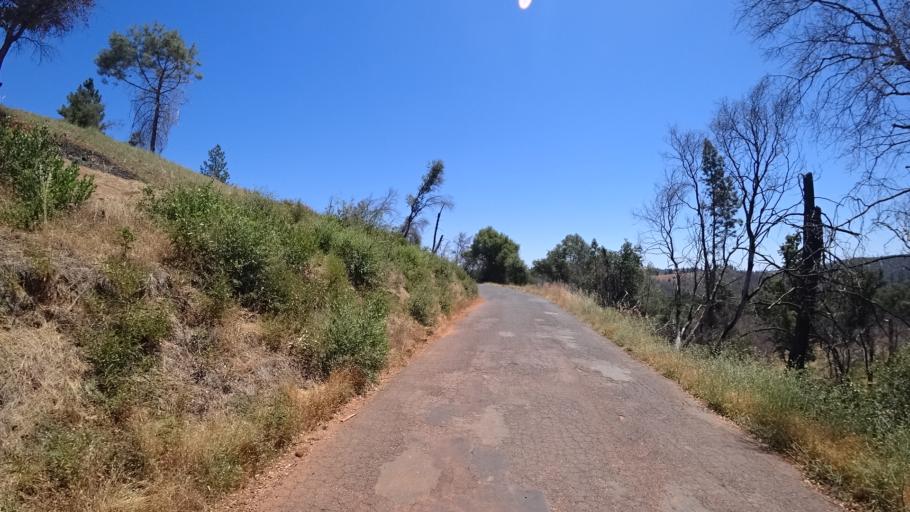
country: US
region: California
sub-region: Calaveras County
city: Mountain Ranch
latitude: 38.2376
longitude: -120.5766
